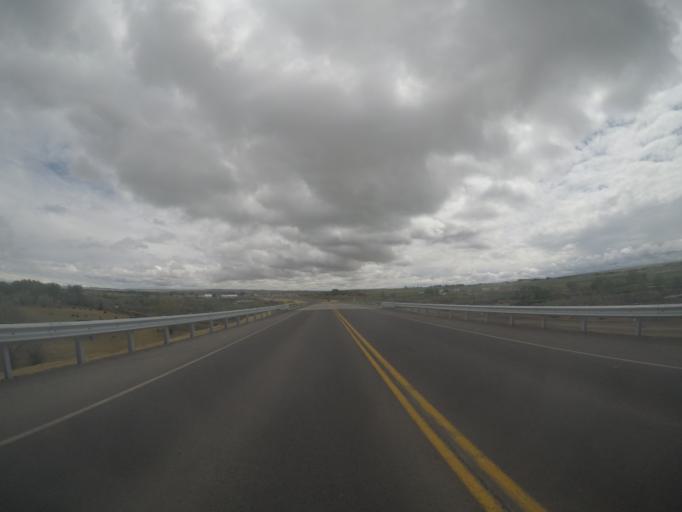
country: US
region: Wyoming
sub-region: Big Horn County
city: Lovell
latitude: 44.8503
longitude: -108.4446
